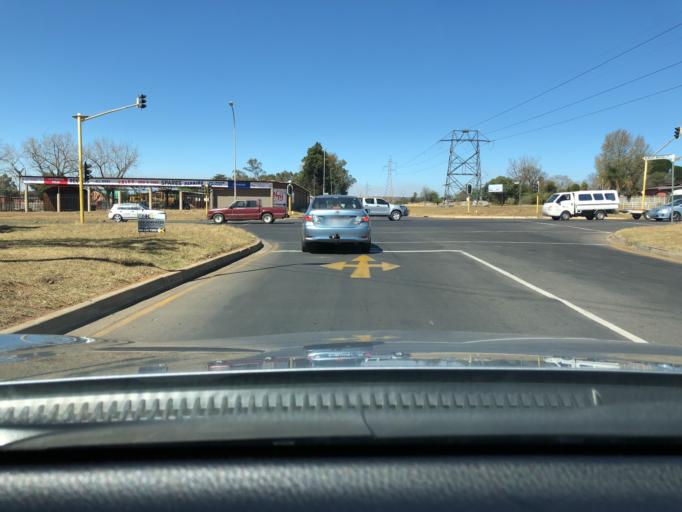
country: ZA
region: KwaZulu-Natal
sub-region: Amajuba District Municipality
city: Newcastle
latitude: -27.7626
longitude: 29.9533
